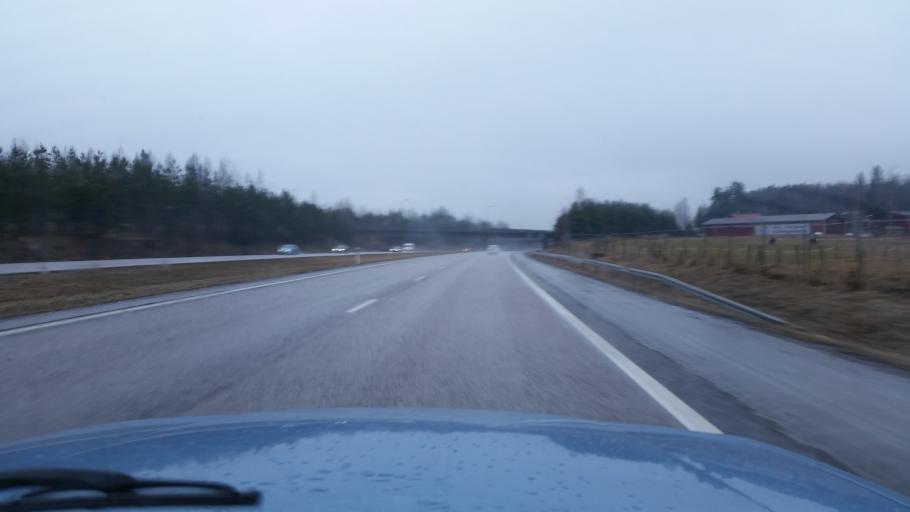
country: FI
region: Uusimaa
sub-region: Helsinki
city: Hyvinge
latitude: 60.5859
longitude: 24.7993
